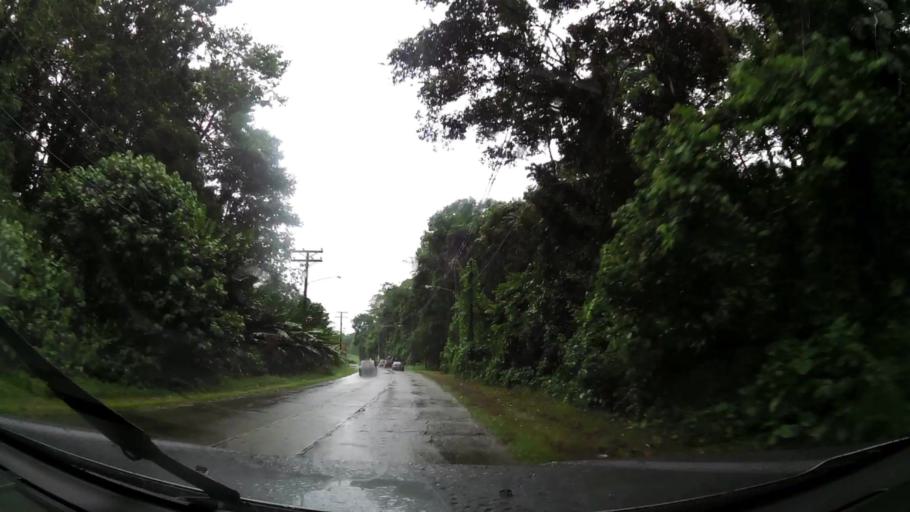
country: PA
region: Colon
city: Las Margaritas
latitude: 9.3207
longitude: -79.8828
